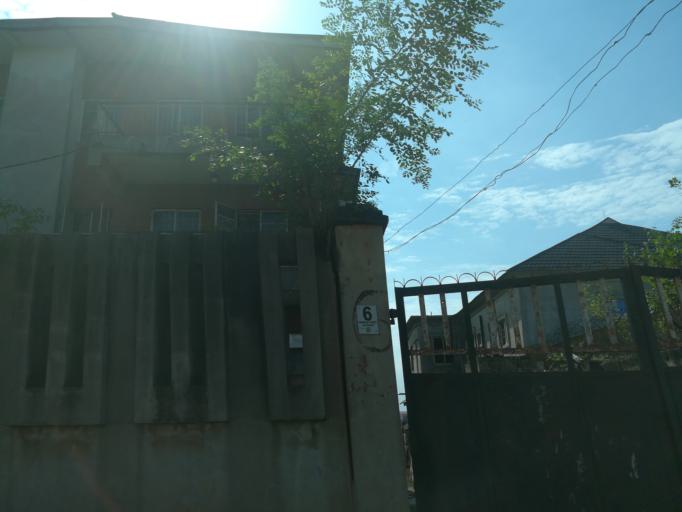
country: NG
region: Lagos
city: Ikorodu
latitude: 6.6057
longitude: 3.5060
